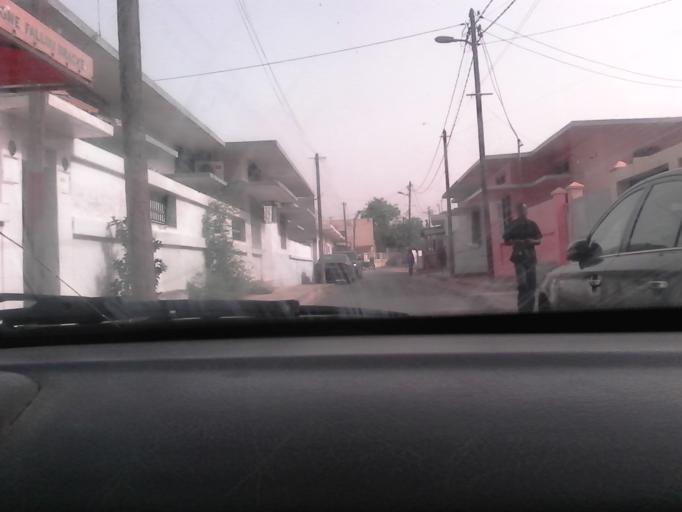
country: SN
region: Dakar
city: Grand Dakar
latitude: 14.7032
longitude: -17.4532
